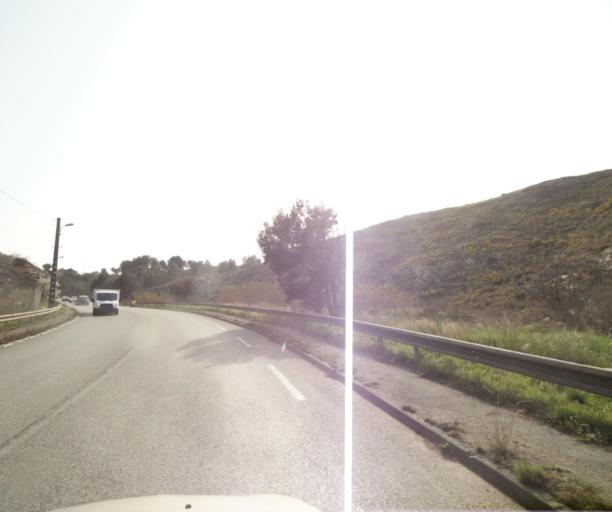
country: FR
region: Provence-Alpes-Cote d'Azur
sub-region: Departement des Bouches-du-Rhone
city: Les Pennes-Mirabeau
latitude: 43.4042
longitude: 5.3323
